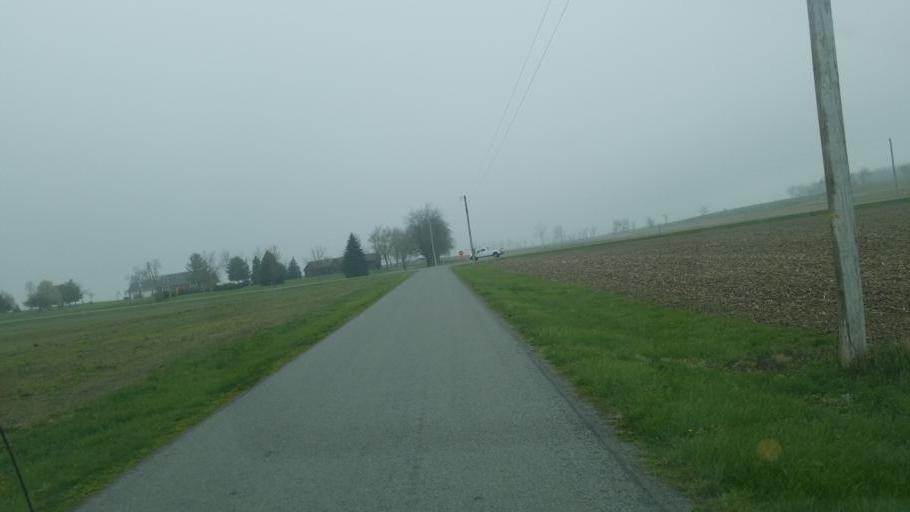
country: US
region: Ohio
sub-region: Logan County
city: Bellefontaine
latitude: 40.4055
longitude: -83.8266
